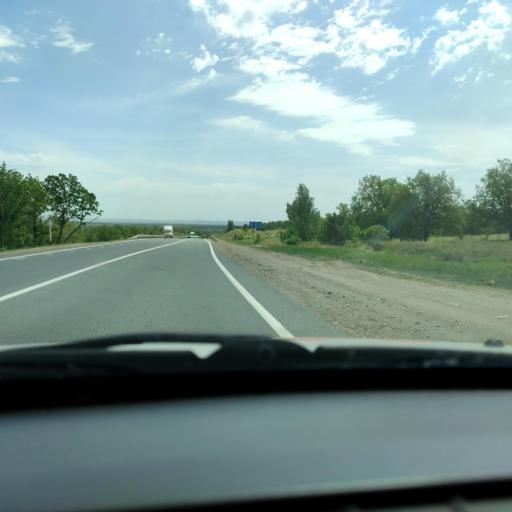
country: RU
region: Samara
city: Mirnyy
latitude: 53.5836
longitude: 50.2852
